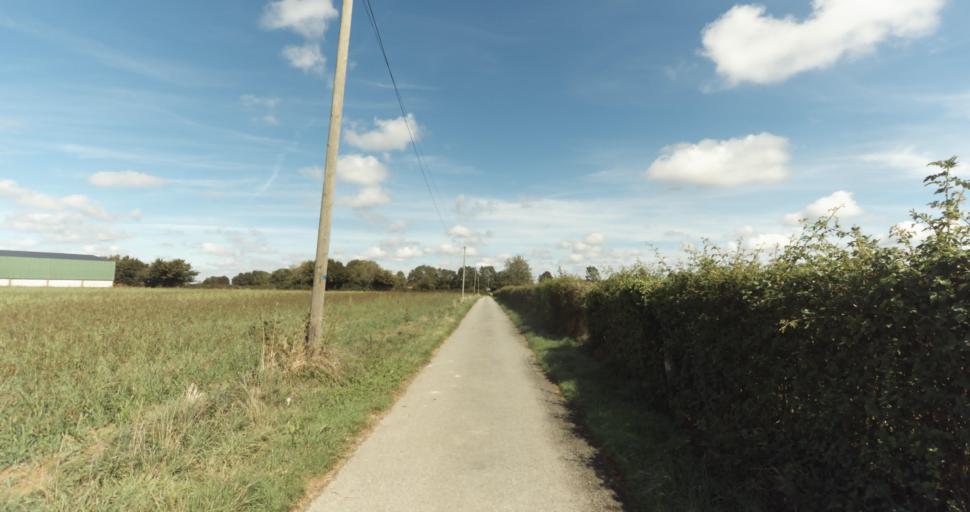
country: FR
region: Lower Normandy
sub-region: Departement du Calvados
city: Orbec
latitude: 48.9410
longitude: 0.3954
